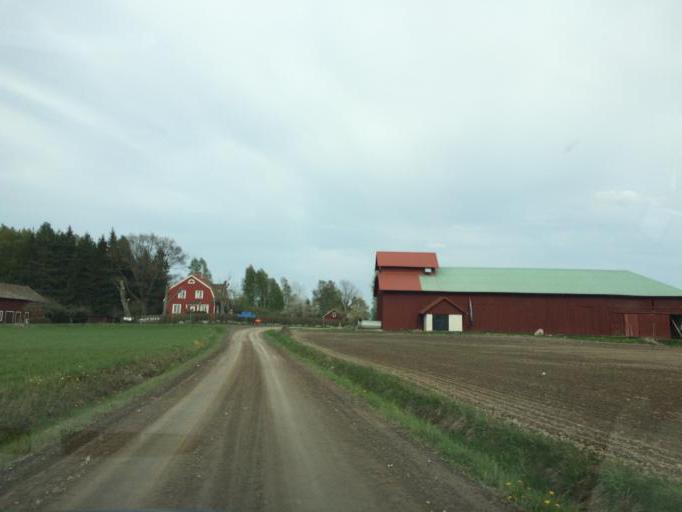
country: SE
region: Vaestmanland
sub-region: Kopings Kommun
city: Koping
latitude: 59.6089
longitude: 16.0743
